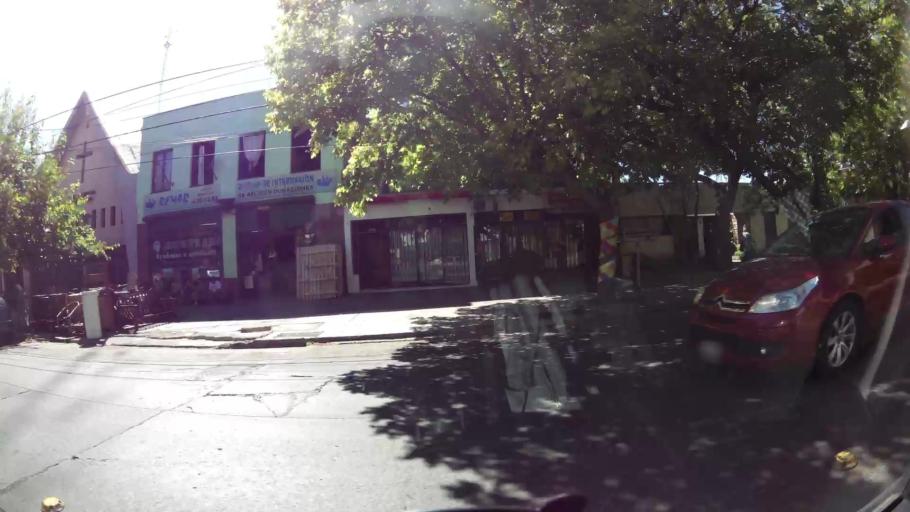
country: AR
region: Mendoza
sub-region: Departamento de Godoy Cruz
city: Godoy Cruz
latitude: -32.9133
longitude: -68.8598
